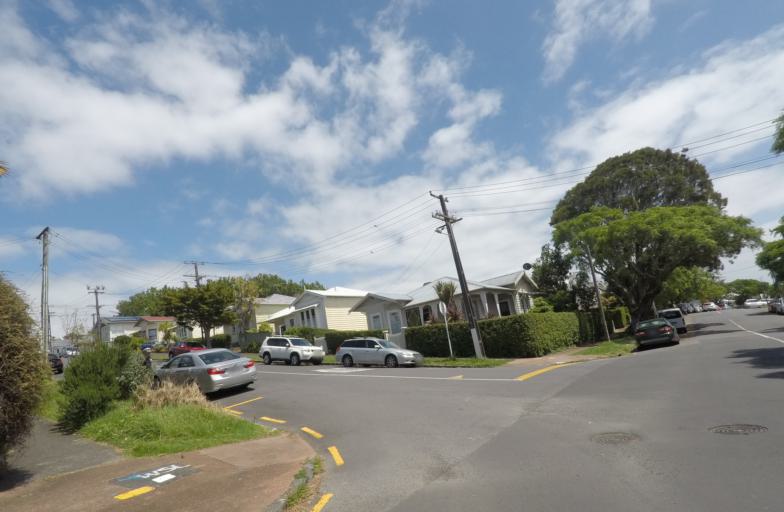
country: NZ
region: Auckland
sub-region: Auckland
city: Auckland
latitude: -36.8619
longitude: 174.7373
